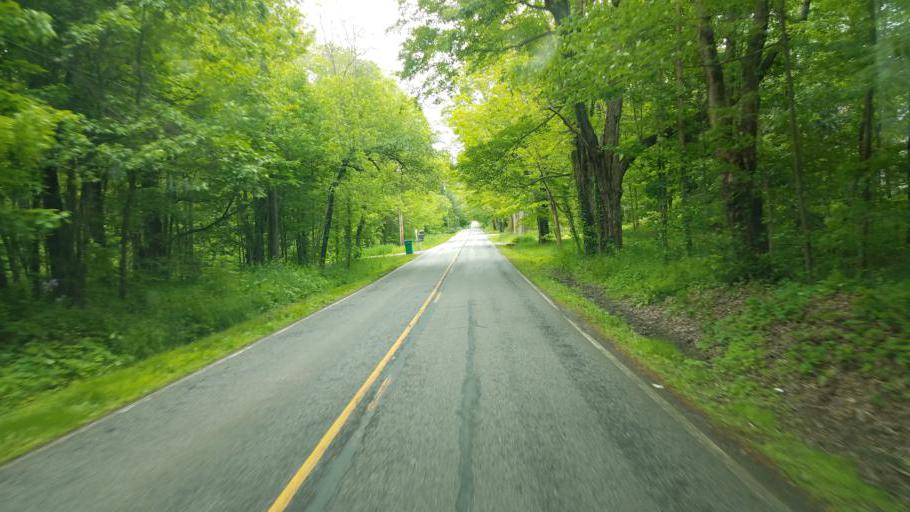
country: US
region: Ohio
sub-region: Geauga County
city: Burton
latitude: 41.4294
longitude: -81.2058
